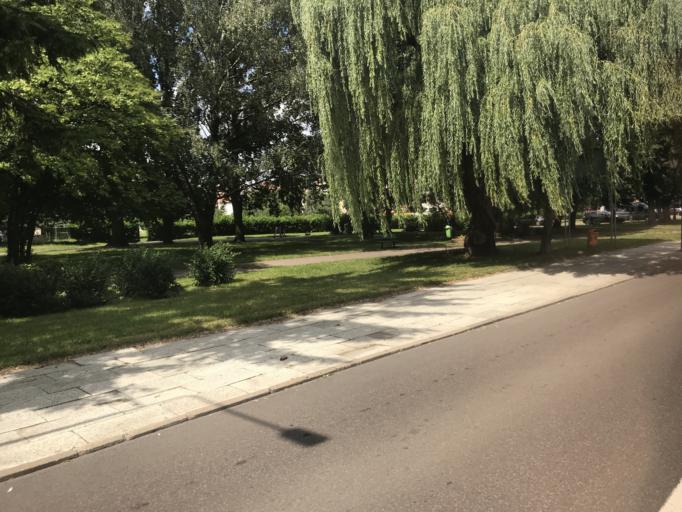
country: PL
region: Warmian-Masurian Voivodeship
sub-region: Powiat elblaski
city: Elblag
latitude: 54.1564
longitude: 19.3986
